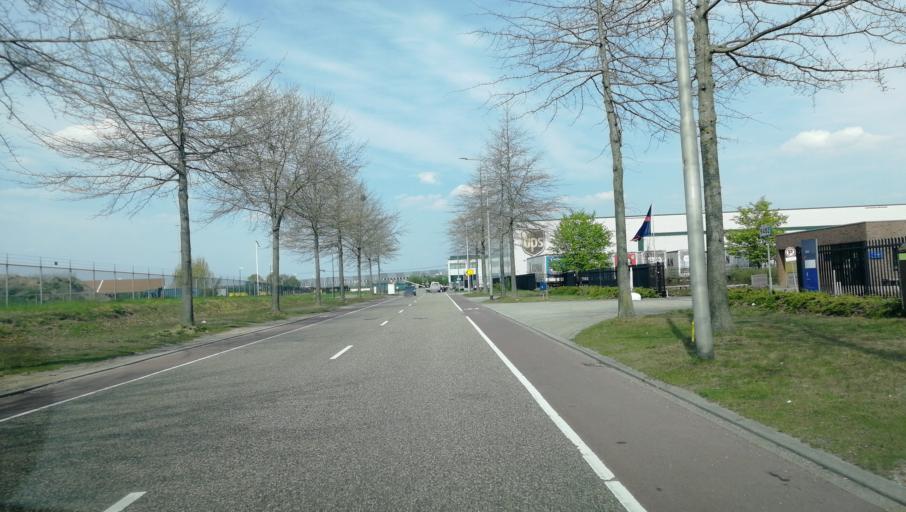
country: NL
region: Limburg
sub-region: Gemeente Peel en Maas
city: Maasbree
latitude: 51.4021
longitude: 6.0850
